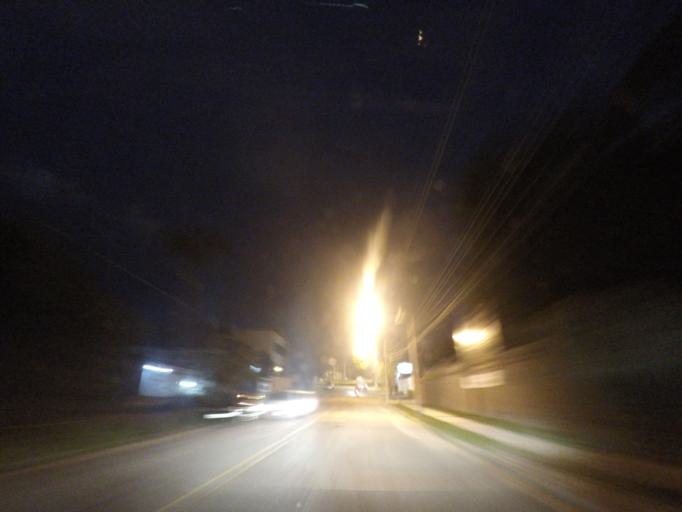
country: BR
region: Parana
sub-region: Curitiba
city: Curitiba
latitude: -25.4070
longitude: -49.2669
